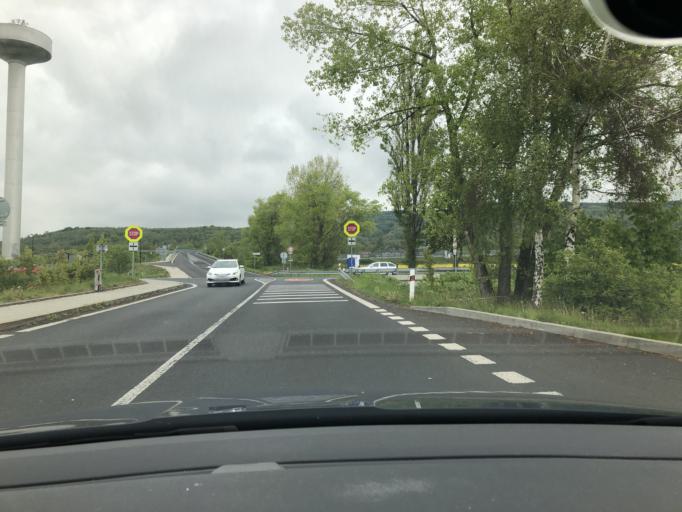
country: CZ
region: Ustecky
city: Libouchec
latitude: 50.7298
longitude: 14.0094
